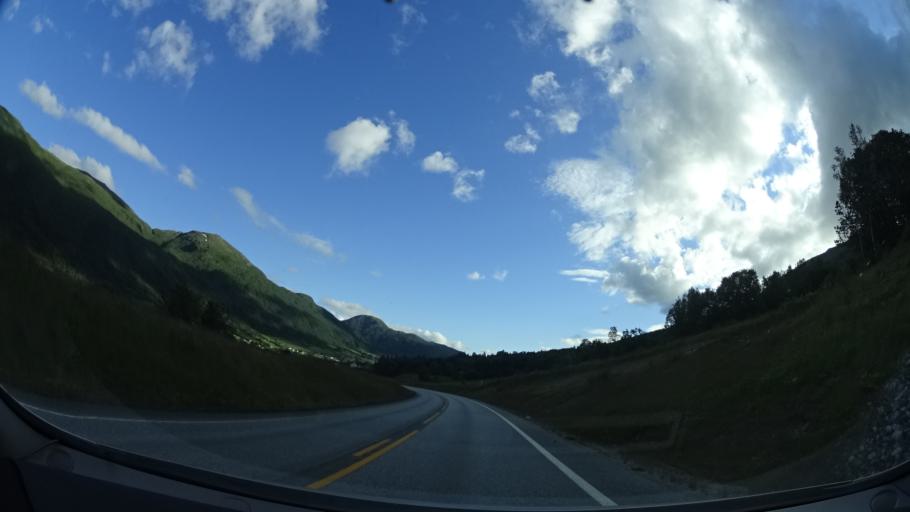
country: NO
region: More og Romsdal
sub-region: Gjemnes
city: Batnfjordsora
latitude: 62.9056
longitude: 7.6776
